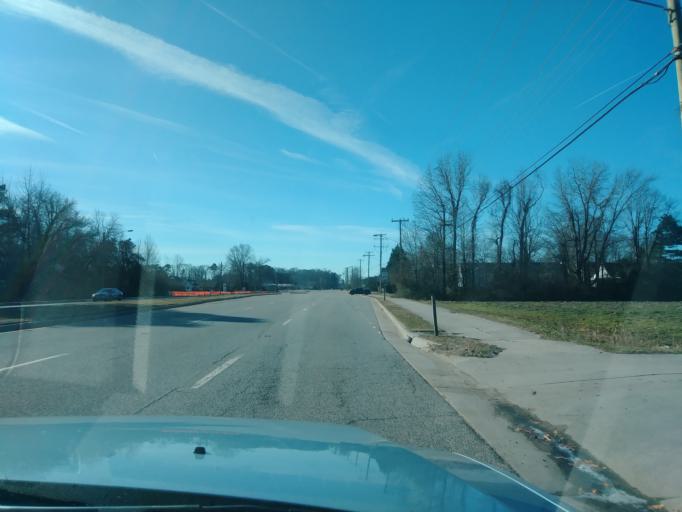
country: US
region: Virginia
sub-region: City of Chesapeake
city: Chesapeake
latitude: 36.7607
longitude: -76.2046
